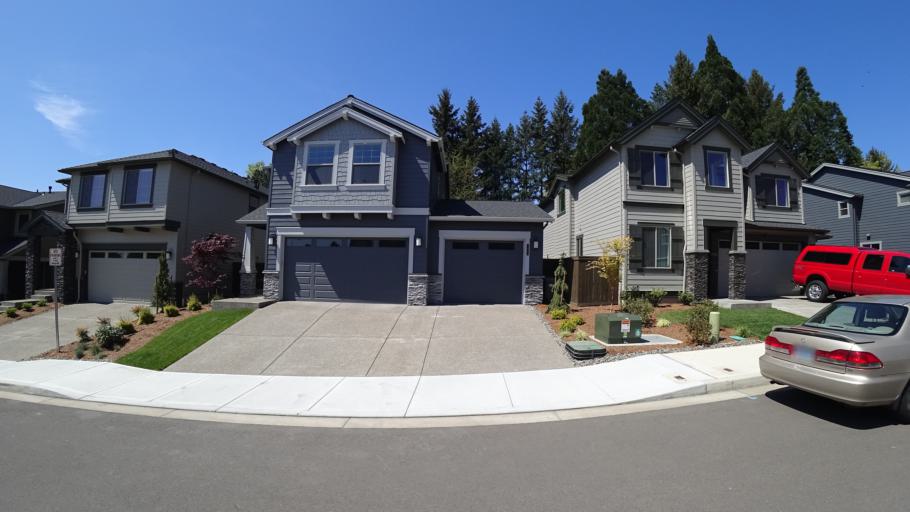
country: US
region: Oregon
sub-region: Washington County
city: Hillsboro
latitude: 45.5100
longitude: -122.9776
